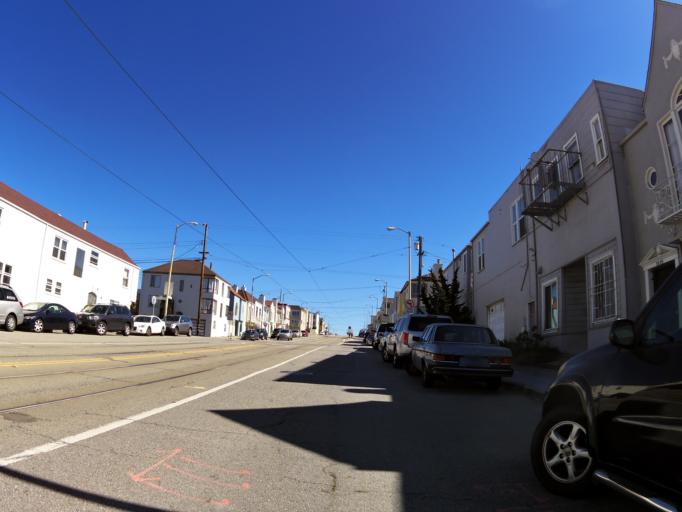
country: US
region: California
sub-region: San Mateo County
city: Daly City
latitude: 37.7609
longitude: -122.4947
